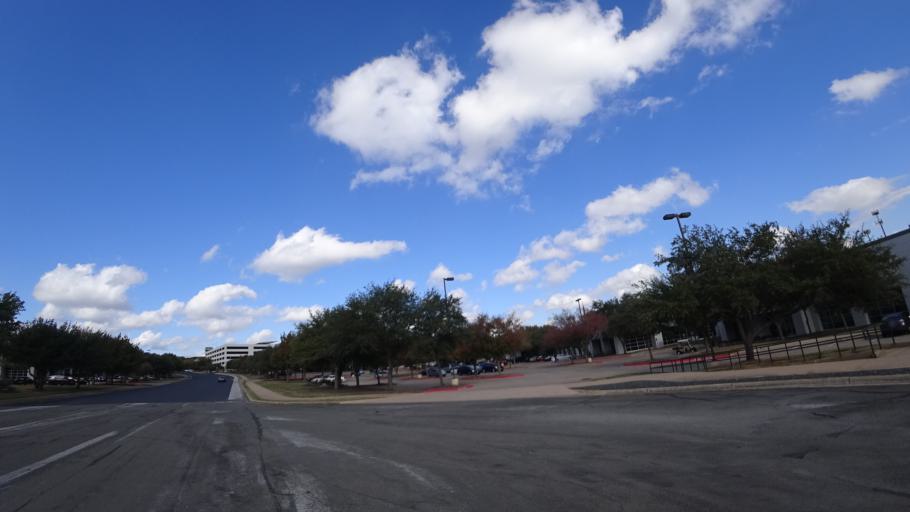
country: US
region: Texas
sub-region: Williamson County
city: Jollyville
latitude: 30.4313
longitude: -97.7309
